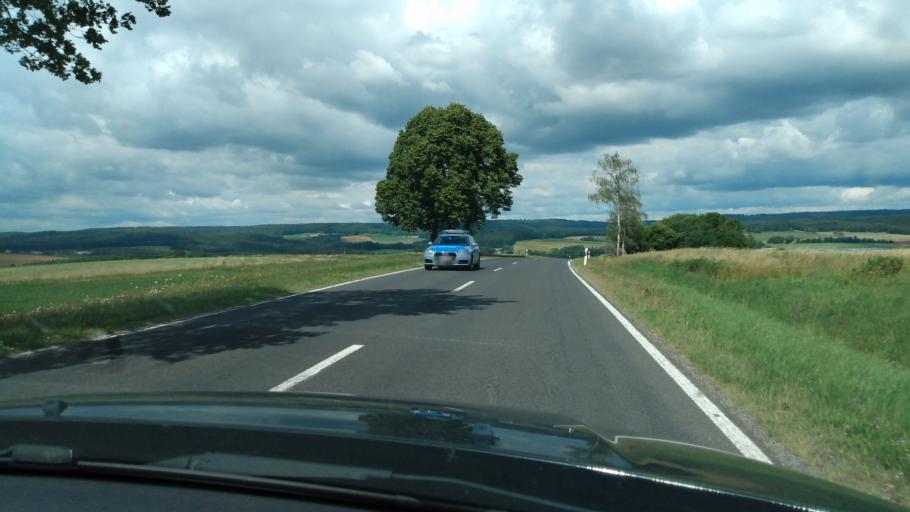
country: DE
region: Rheinland-Pfalz
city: Musweiler
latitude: 50.0181
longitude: 6.8103
